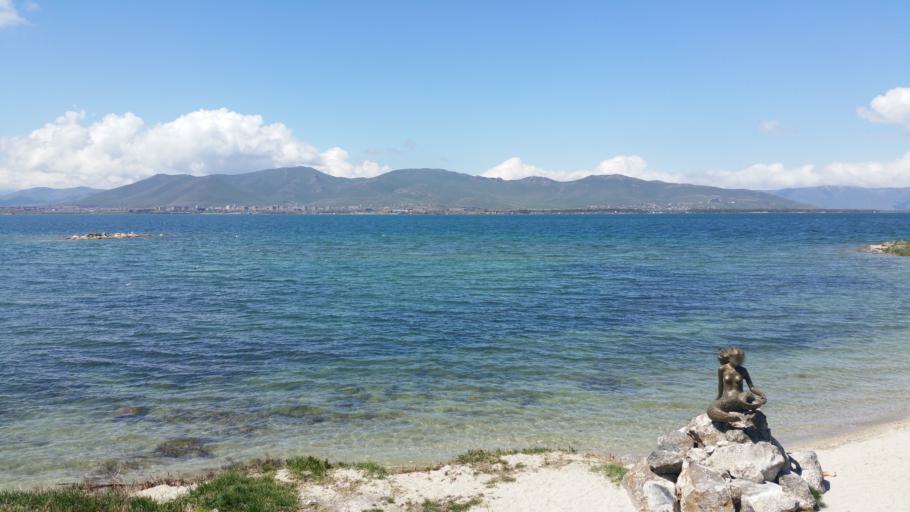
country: AM
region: Geghark'unik'i Marz
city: Sevan
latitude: 40.5116
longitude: 44.9858
